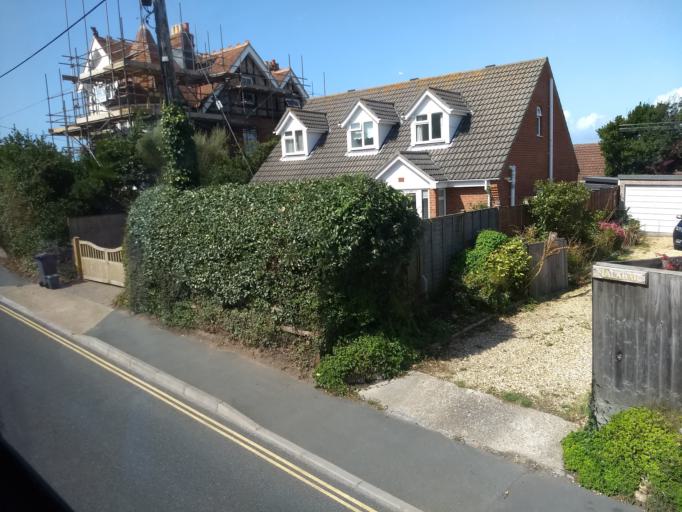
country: GB
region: England
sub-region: Isle of Wight
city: Totland
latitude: 50.6842
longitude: -1.5375
